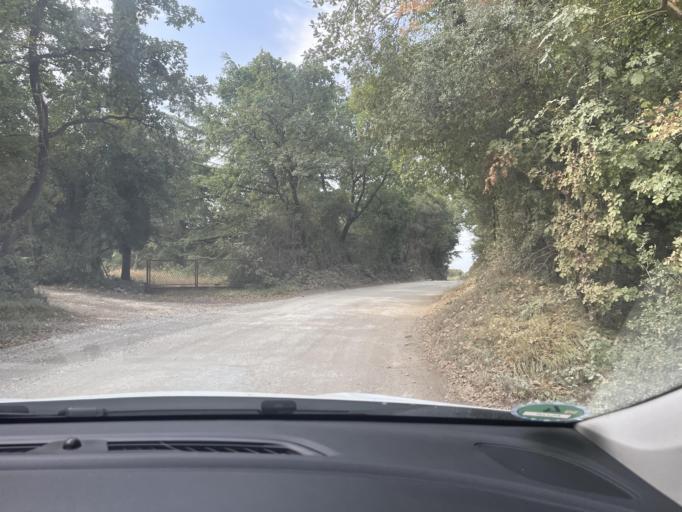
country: HR
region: Istarska
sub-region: Grad Rovinj
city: Rovinj
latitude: 45.0442
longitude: 13.7128
